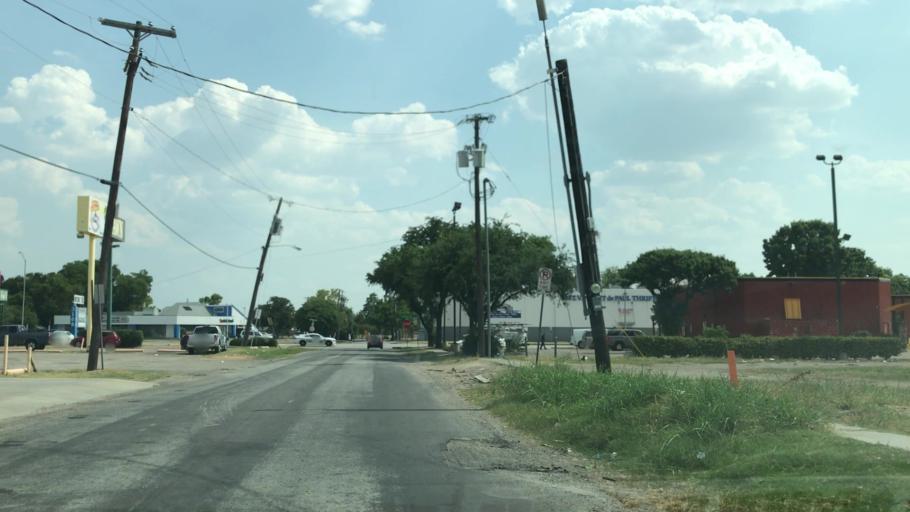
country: US
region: Texas
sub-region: Dallas County
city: University Park
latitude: 32.8561
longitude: -96.8683
